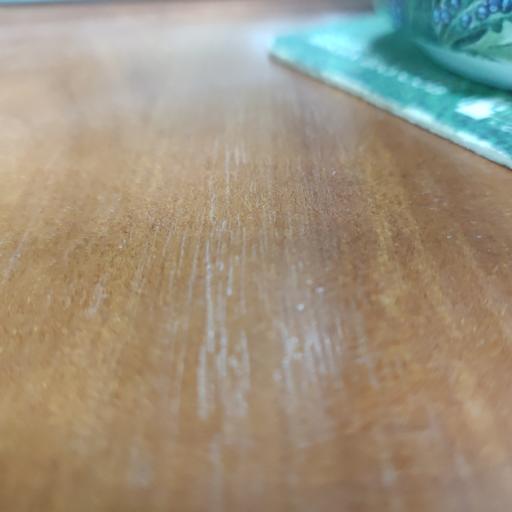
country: RU
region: Brjansk
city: Navlya
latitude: 52.8826
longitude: 34.3766
